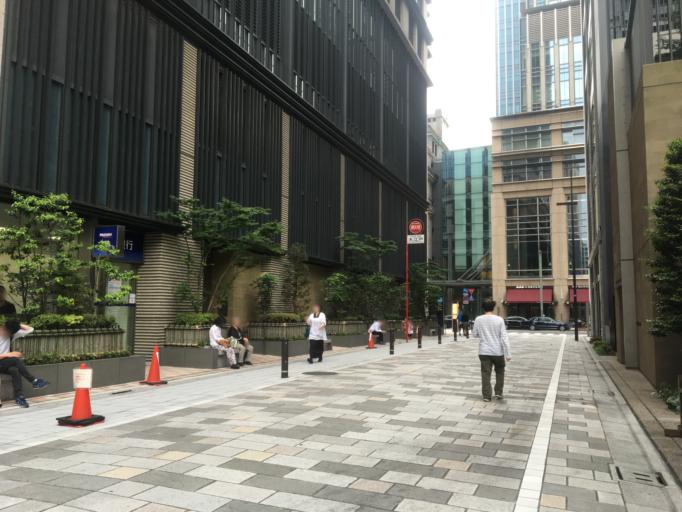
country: JP
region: Tokyo
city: Tokyo
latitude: 35.6869
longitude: 139.7745
